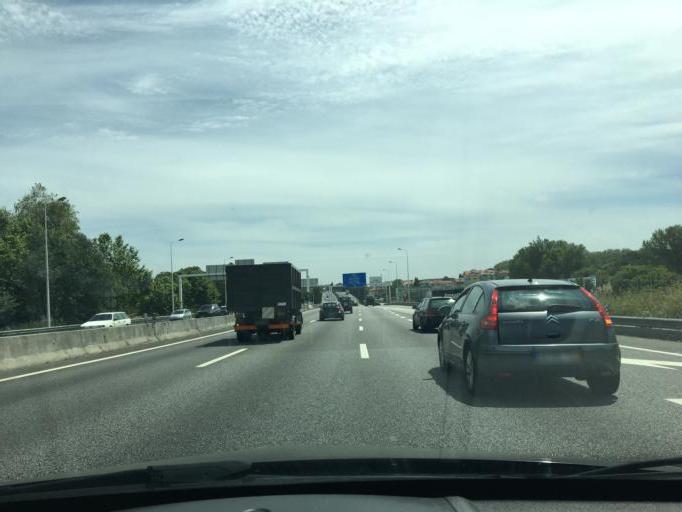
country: PT
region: Porto
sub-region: Porto
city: Porto
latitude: 41.1735
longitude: -8.6211
